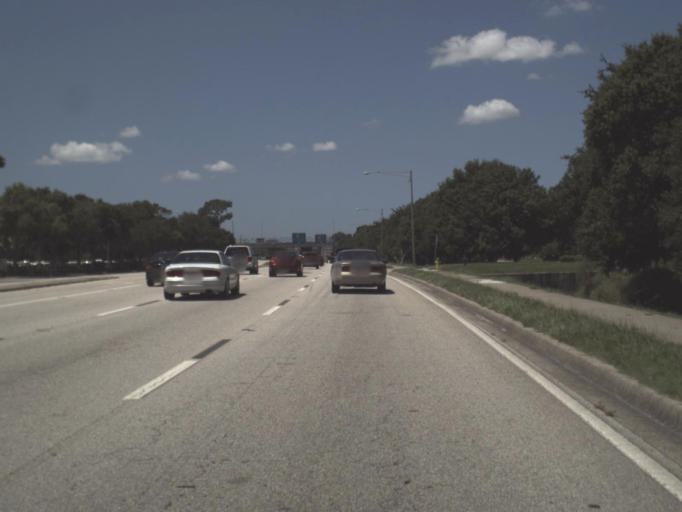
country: US
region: Florida
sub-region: Pinellas County
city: Pinellas Park
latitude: 27.8793
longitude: -82.7058
